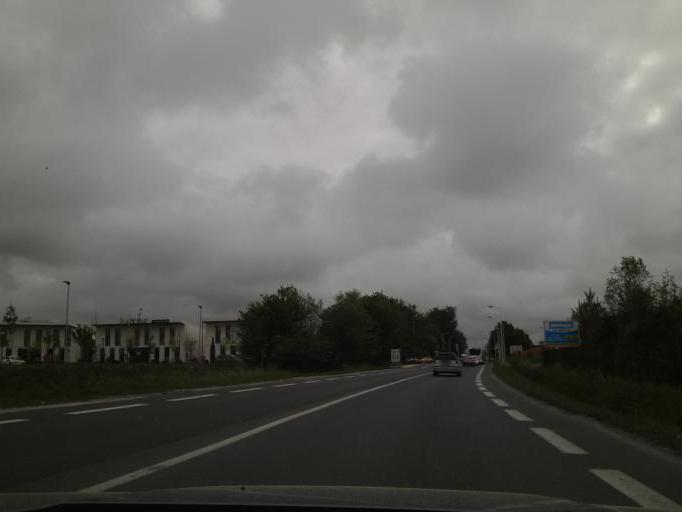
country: FR
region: Aquitaine
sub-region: Departement de la Gironde
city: Le Haillan
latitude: 44.8588
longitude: -0.6749
